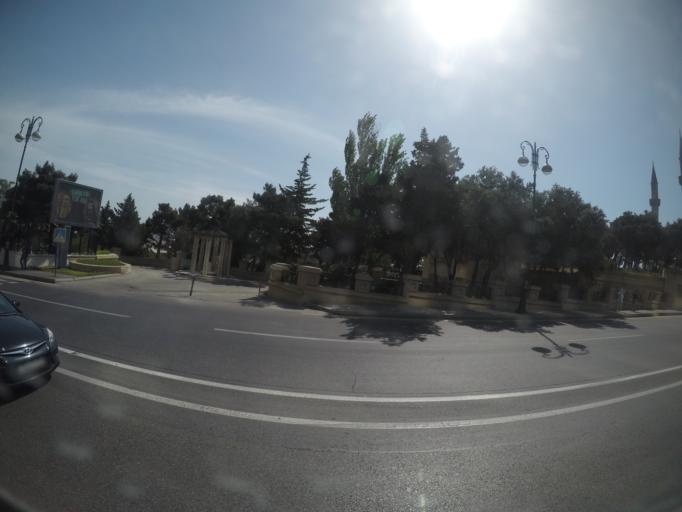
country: AZ
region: Baki
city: Badamdar
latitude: 40.3591
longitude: 49.8275
